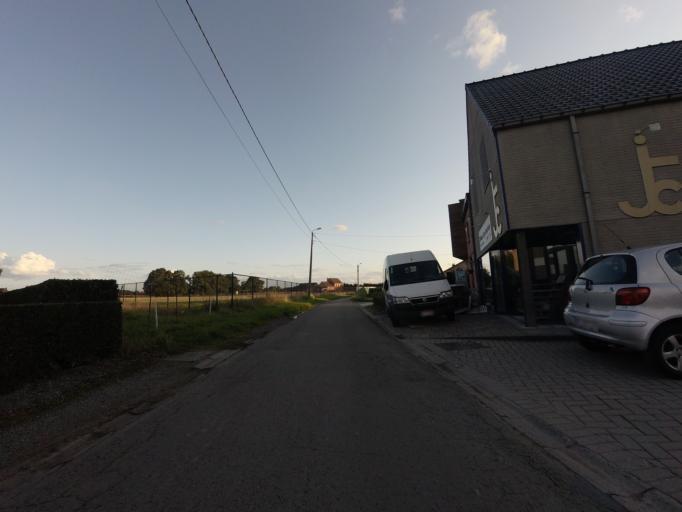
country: BE
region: Flanders
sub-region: Provincie Vlaams-Brabant
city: Londerzeel
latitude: 51.0022
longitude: 4.3195
